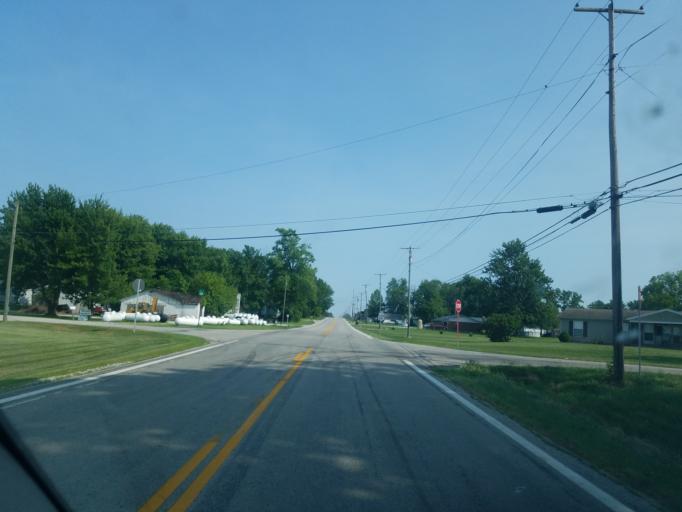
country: US
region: Ohio
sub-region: Wyandot County
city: Carey
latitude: 41.0291
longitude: -83.2983
